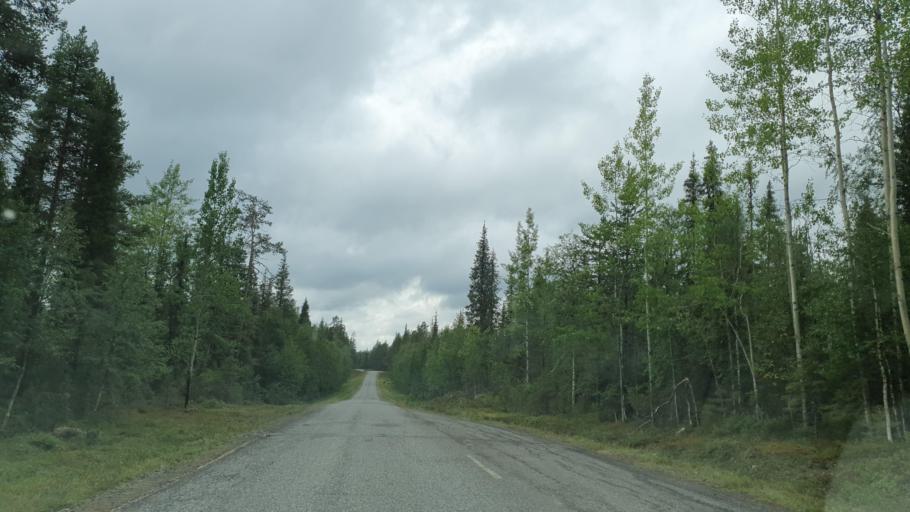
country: FI
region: Lapland
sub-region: Tunturi-Lappi
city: Muonio
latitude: 67.7351
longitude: 24.2725
